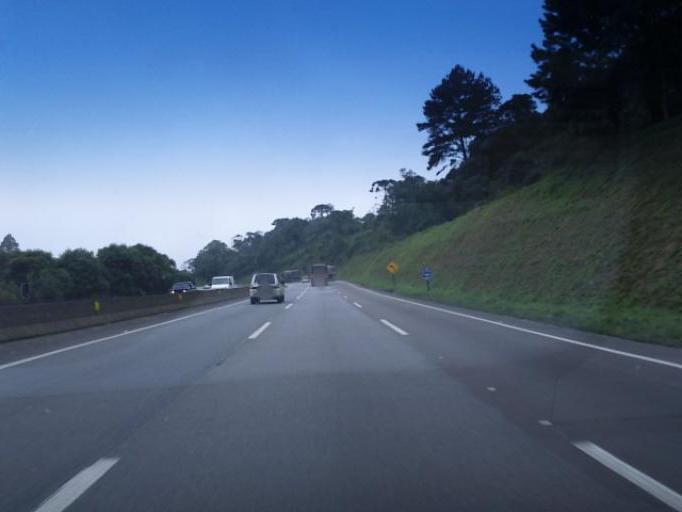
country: BR
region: Parana
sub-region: Sao Jose Dos Pinhais
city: Sao Jose dos Pinhais
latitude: -25.8457
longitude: -49.0711
